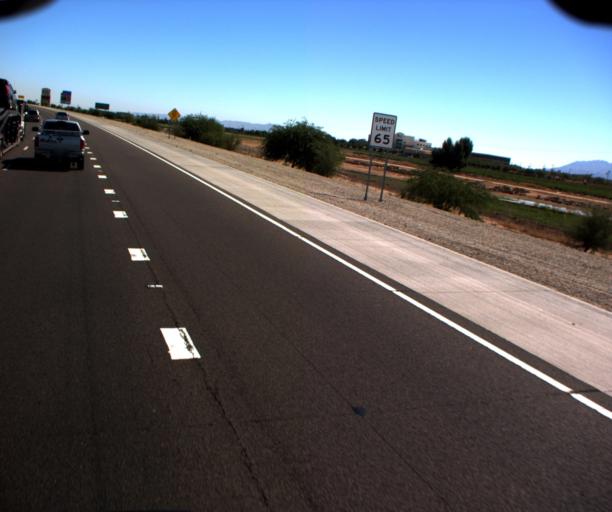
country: US
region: Arizona
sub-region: Maricopa County
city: Goodyear
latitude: 33.4583
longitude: -112.3693
